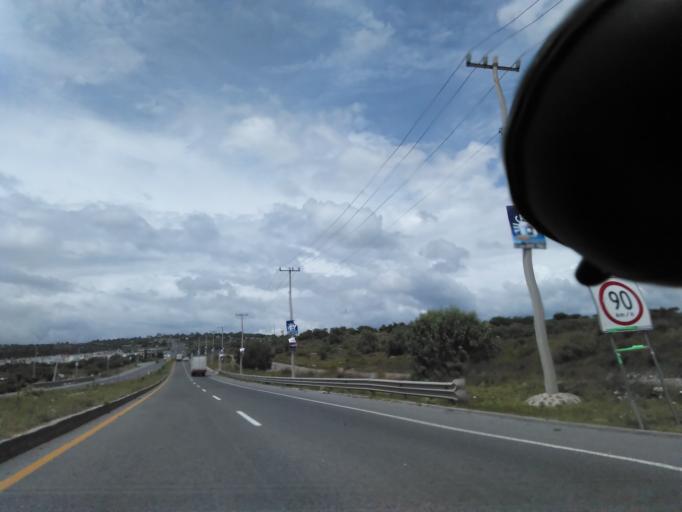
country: MX
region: Hidalgo
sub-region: Atotonilco de Tula
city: Paseos de la Pradera
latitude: 19.9163
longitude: -99.2389
